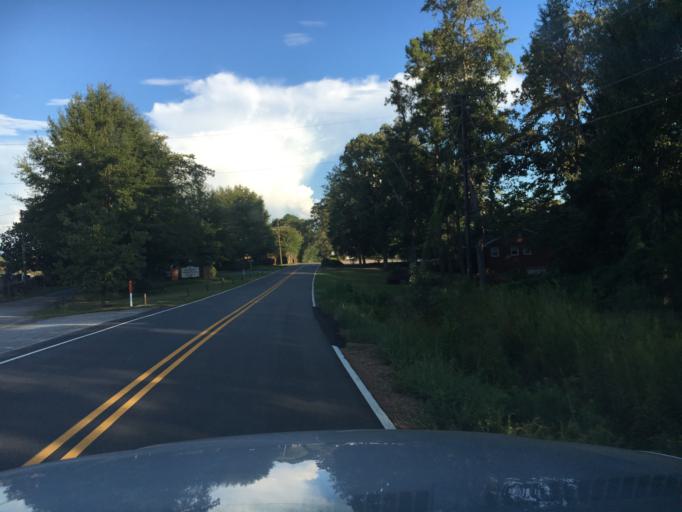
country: US
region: South Carolina
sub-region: Spartanburg County
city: Fairforest
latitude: 34.8974
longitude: -82.0321
